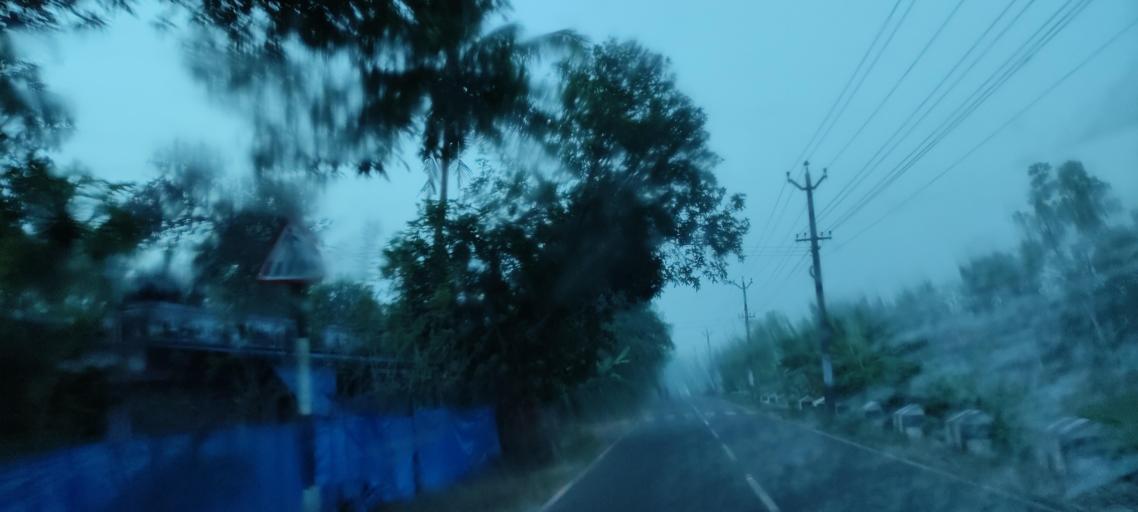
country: IN
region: Kerala
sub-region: Alappuzha
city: Alleppey
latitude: 9.5740
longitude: 76.3311
